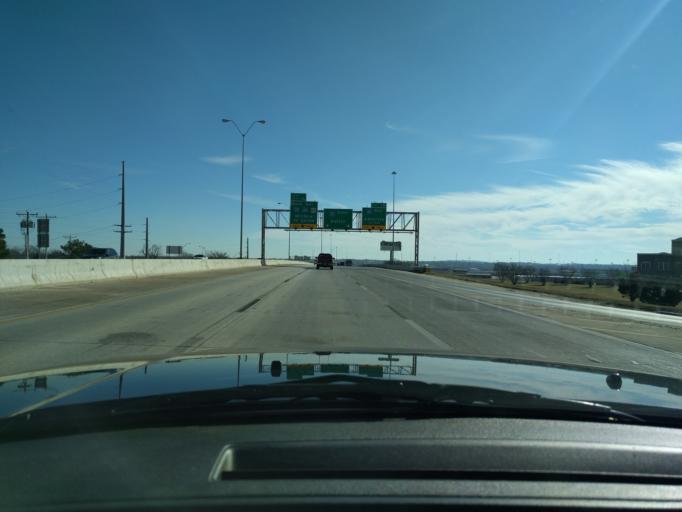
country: US
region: Oklahoma
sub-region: Oklahoma County
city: Oklahoma City
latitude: 35.4709
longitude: -97.5046
